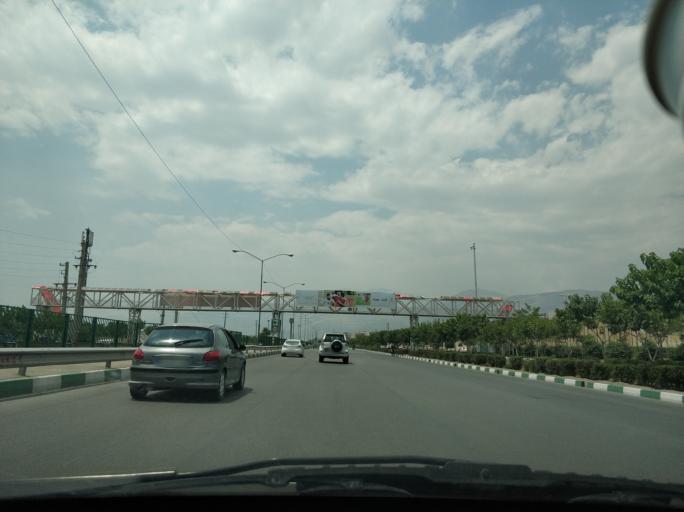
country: IR
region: Tehran
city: Tajrish
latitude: 35.7610
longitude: 51.5711
